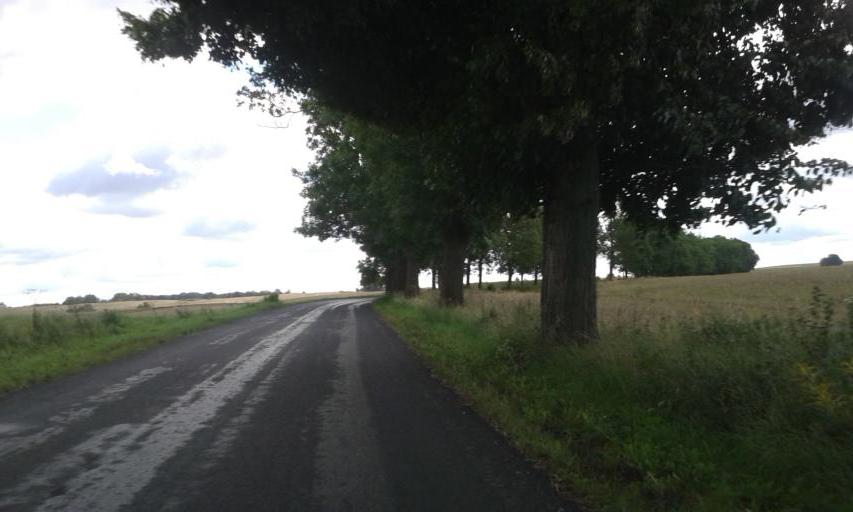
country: PL
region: West Pomeranian Voivodeship
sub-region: Powiat walecki
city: Walcz
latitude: 53.2292
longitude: 16.5426
